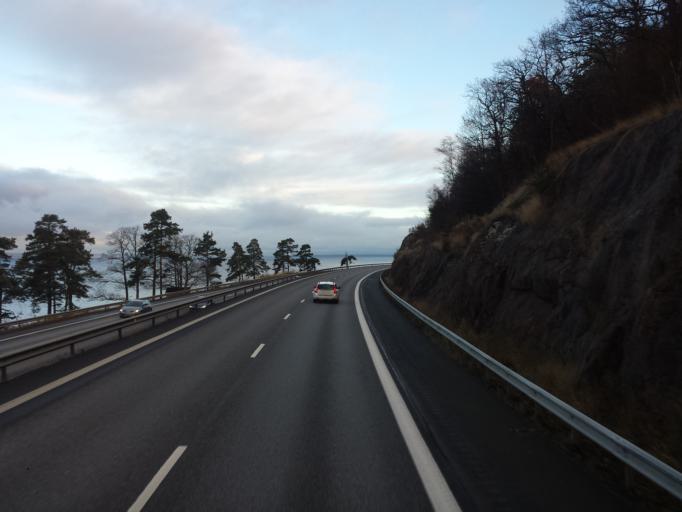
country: SE
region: Joenkoeping
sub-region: Jonkopings Kommun
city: Kaxholmen
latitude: 57.8628
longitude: 14.2681
